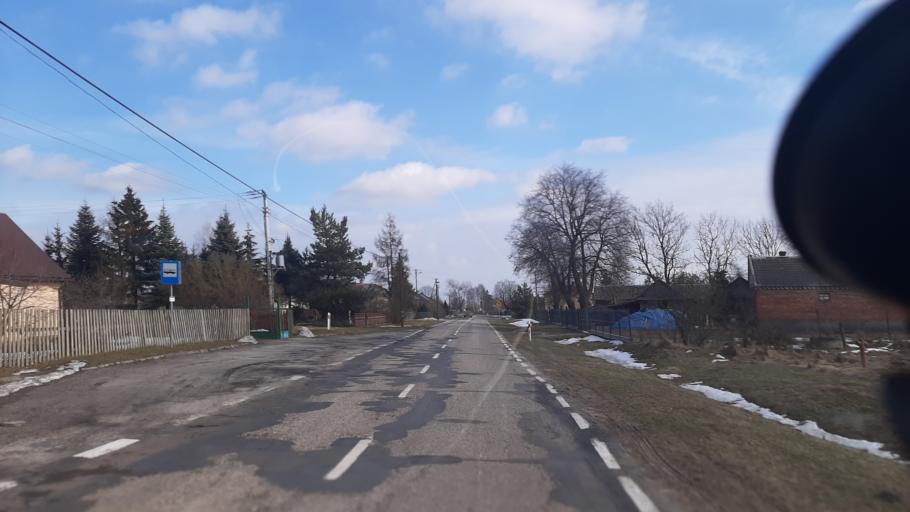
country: PL
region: Lublin Voivodeship
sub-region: Powiat wlodawski
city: Urszulin
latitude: 51.4934
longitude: 23.2317
